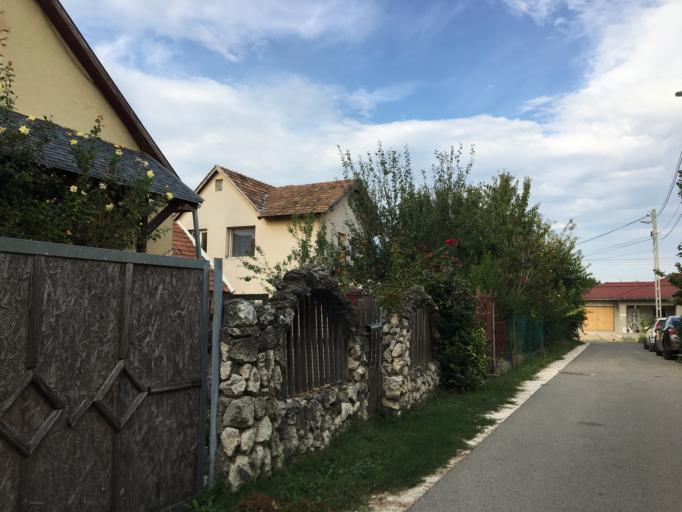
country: HU
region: Pest
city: Szigetszentmiklos
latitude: 47.3546
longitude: 19.0287
